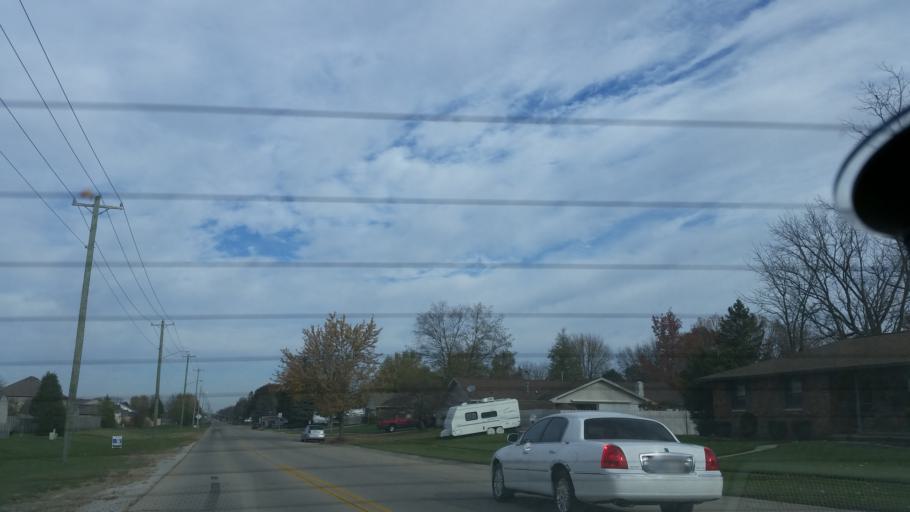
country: US
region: Indiana
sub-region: Howard County
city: Indian Heights
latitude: 40.4475
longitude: -86.1556
